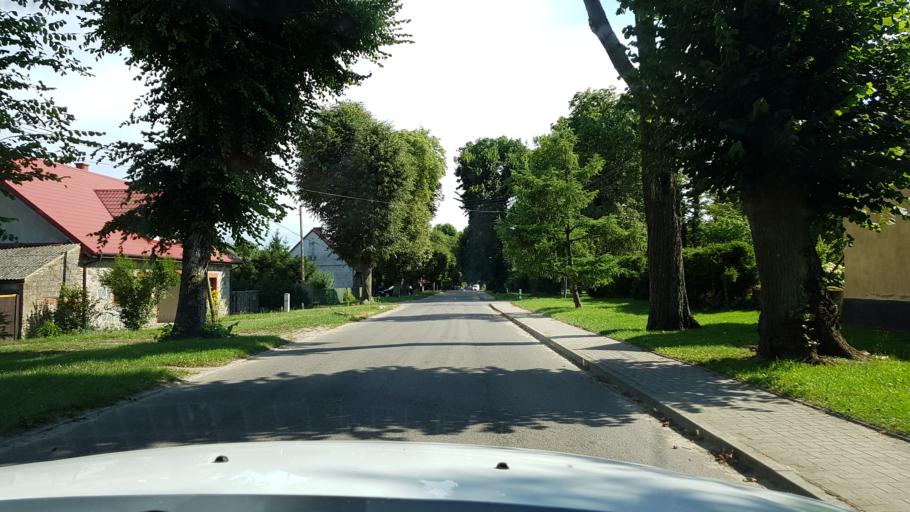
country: PL
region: West Pomeranian Voivodeship
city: Trzcinsko Zdroj
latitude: 52.9552
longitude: 14.5490
